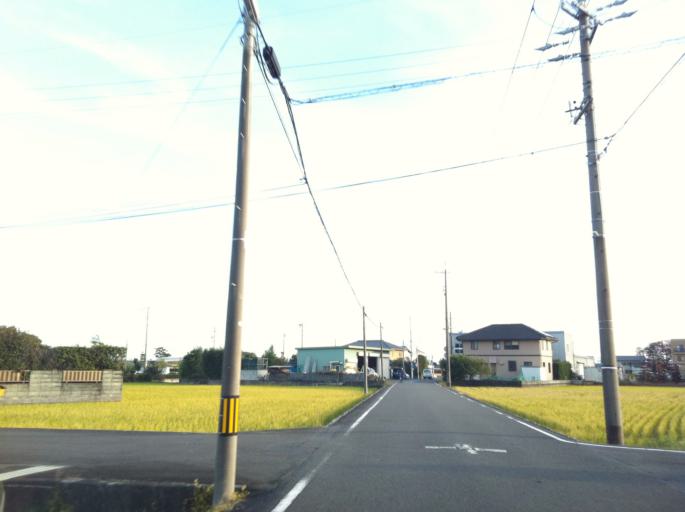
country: JP
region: Shizuoka
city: Yaizu
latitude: 34.8356
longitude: 138.2993
